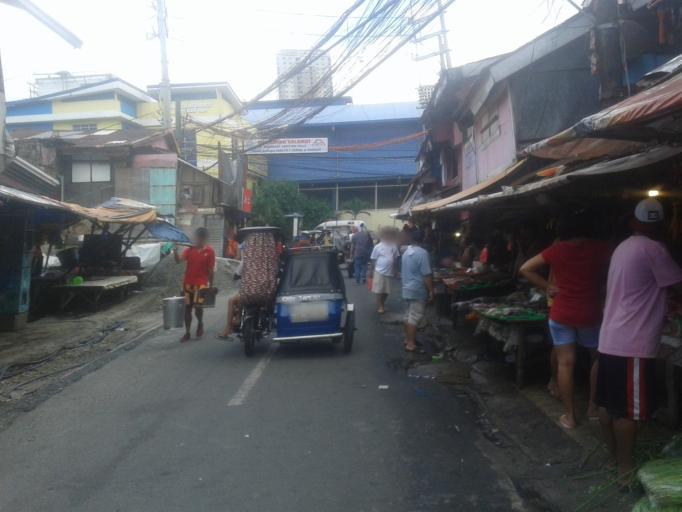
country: PH
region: Metro Manila
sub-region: Mandaluyong
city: Mandaluyong City
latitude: 14.5860
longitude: 121.0413
